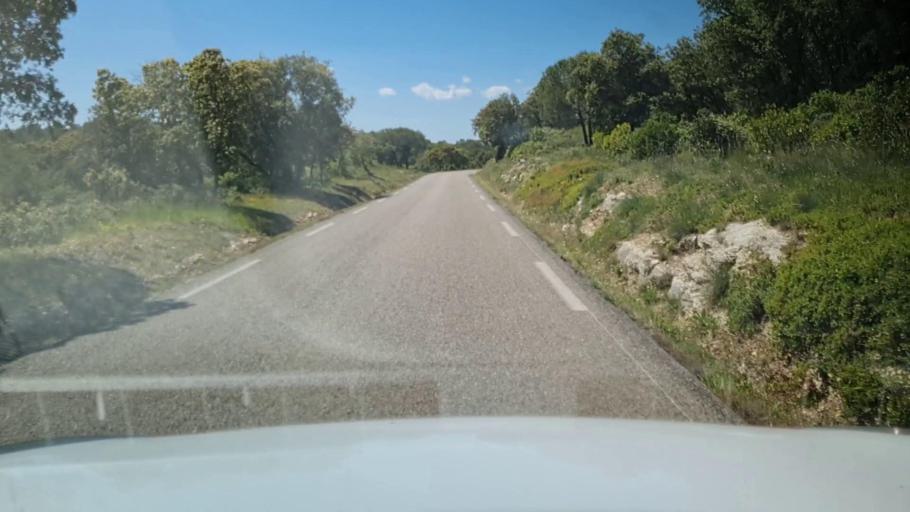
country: FR
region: Languedoc-Roussillon
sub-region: Departement du Gard
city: Clarensac
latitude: 43.8438
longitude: 4.2306
